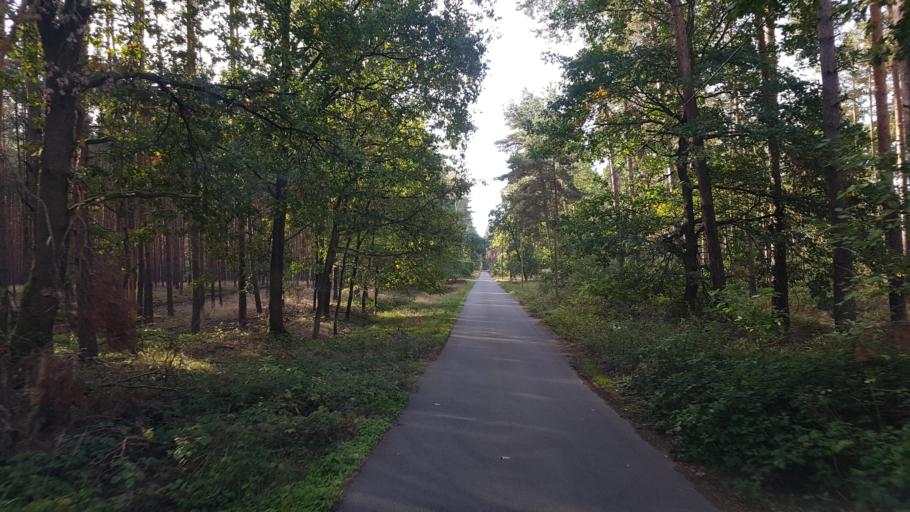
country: DE
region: Brandenburg
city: Drahnsdorf
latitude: 51.8427
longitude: 13.5345
